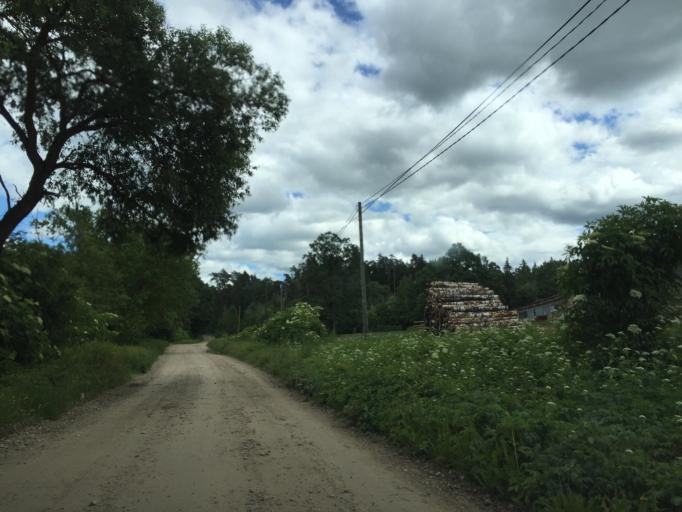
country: LV
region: Lecava
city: Iecava
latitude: 56.5913
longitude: 24.2158
